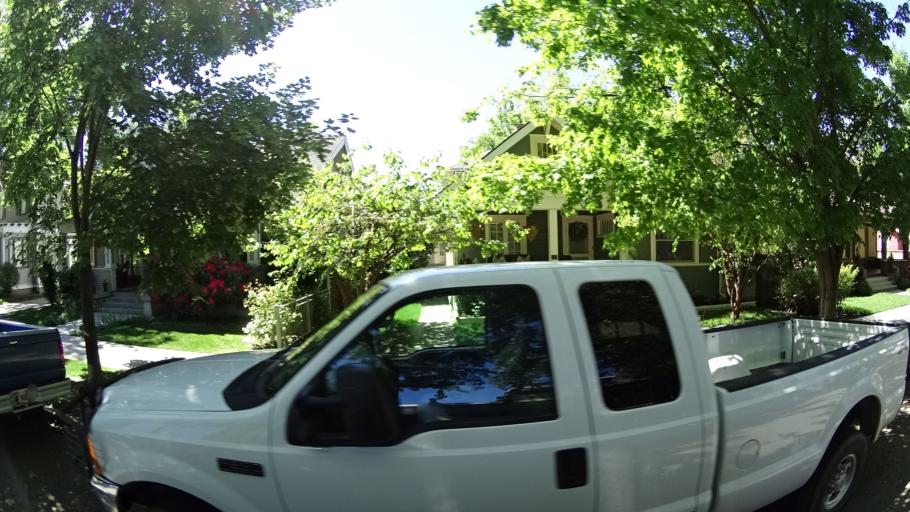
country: US
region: Idaho
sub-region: Ada County
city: Boise
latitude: 43.6267
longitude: -116.2100
